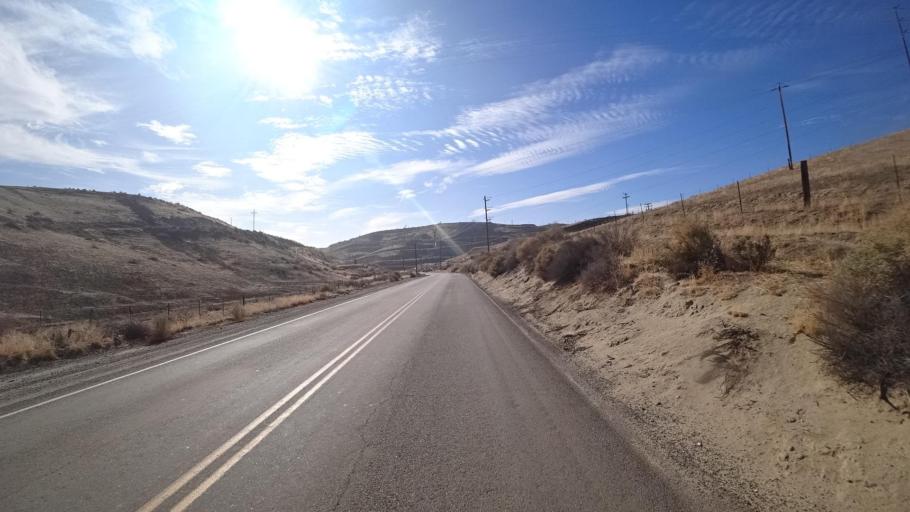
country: US
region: California
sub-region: Kern County
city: Oildale
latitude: 35.5917
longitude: -118.9578
